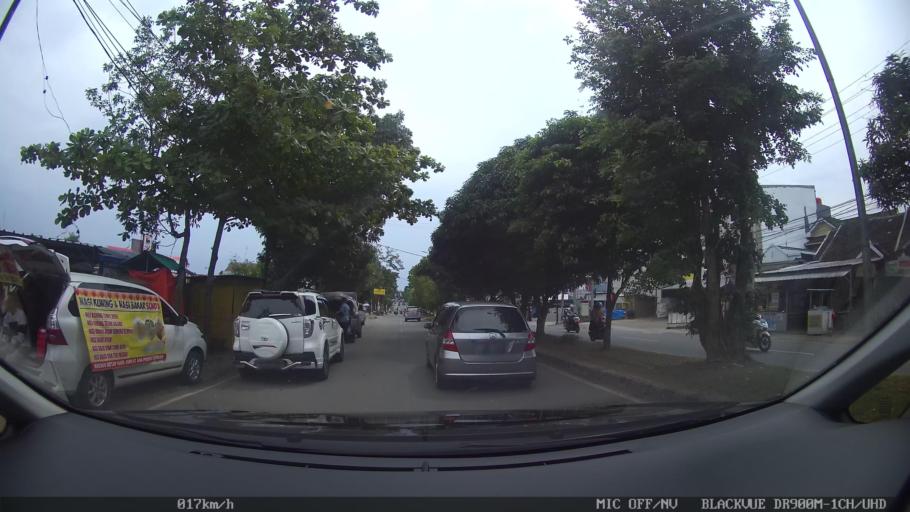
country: ID
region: Lampung
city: Kedaton
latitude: -5.3989
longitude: 105.2118
